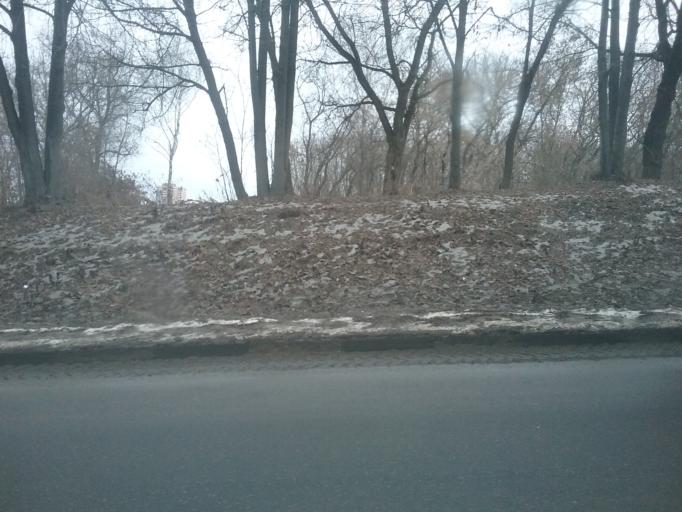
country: RU
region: Tula
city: Tula
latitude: 54.1688
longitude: 37.6410
